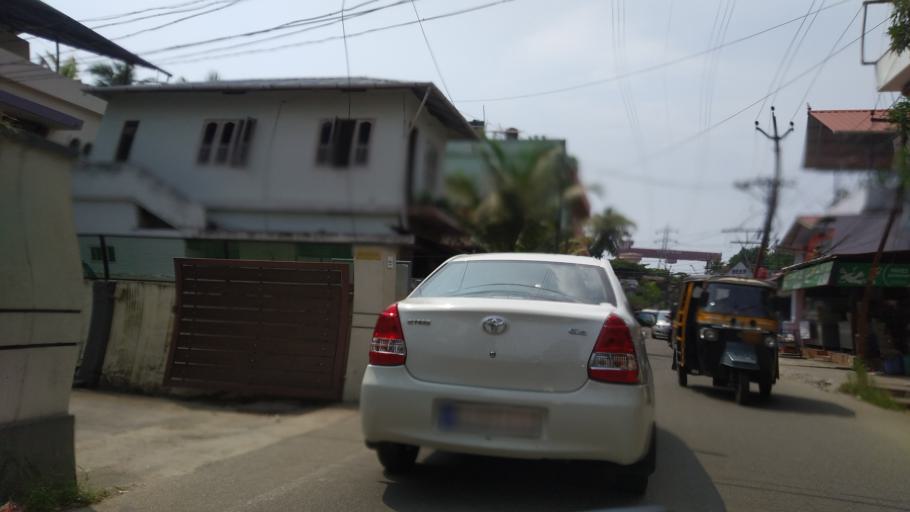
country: IN
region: Kerala
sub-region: Ernakulam
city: Cochin
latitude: 9.9557
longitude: 76.2947
